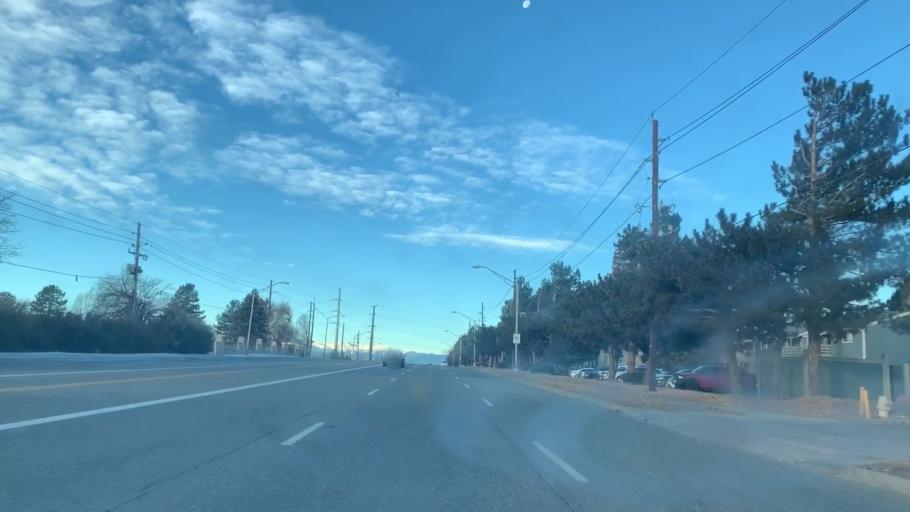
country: US
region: Colorado
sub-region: Arapahoe County
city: Glendale
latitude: 39.6532
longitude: -104.8899
